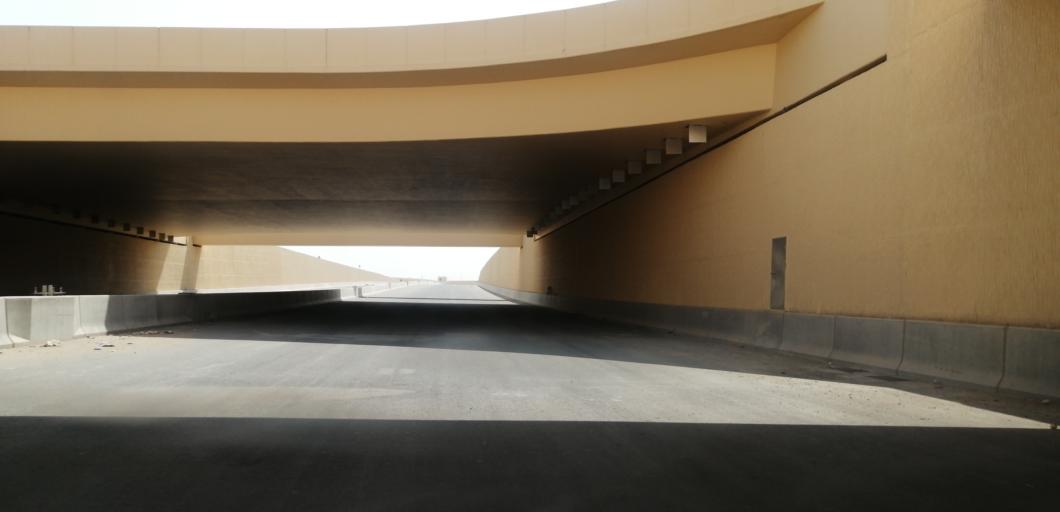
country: KW
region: Muhafazat al Jahra'
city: Al Jahra'
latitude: 29.4529
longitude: 47.5889
